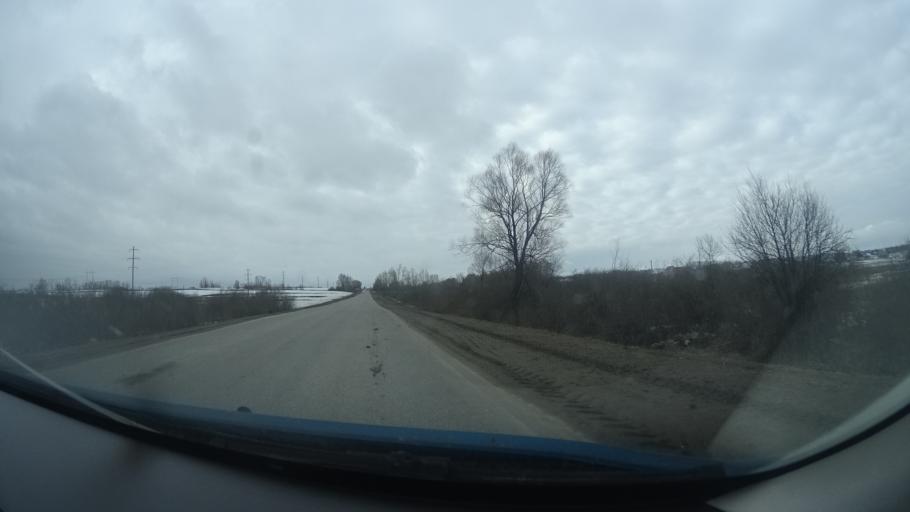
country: RU
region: Bashkortostan
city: Birsk
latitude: 55.4582
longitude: 55.5922
